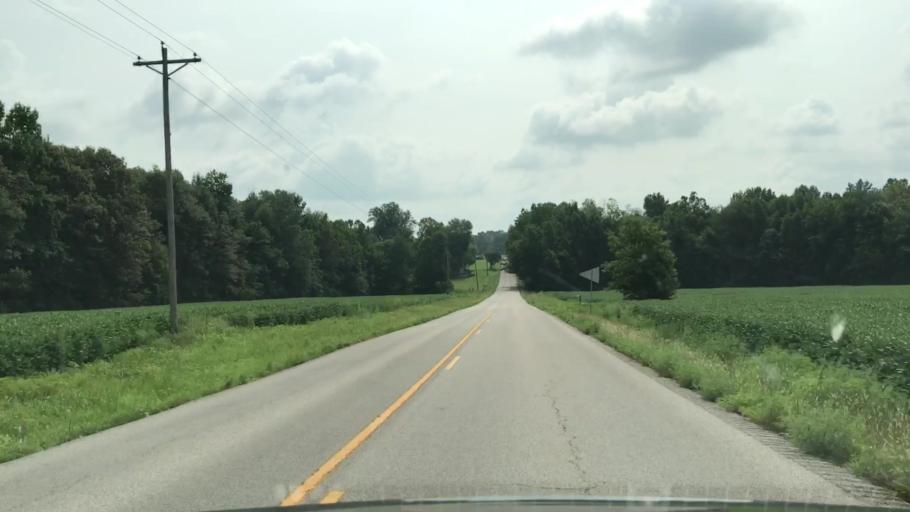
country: US
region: Kentucky
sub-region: Edmonson County
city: Brownsville
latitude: 37.1430
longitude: -86.1888
